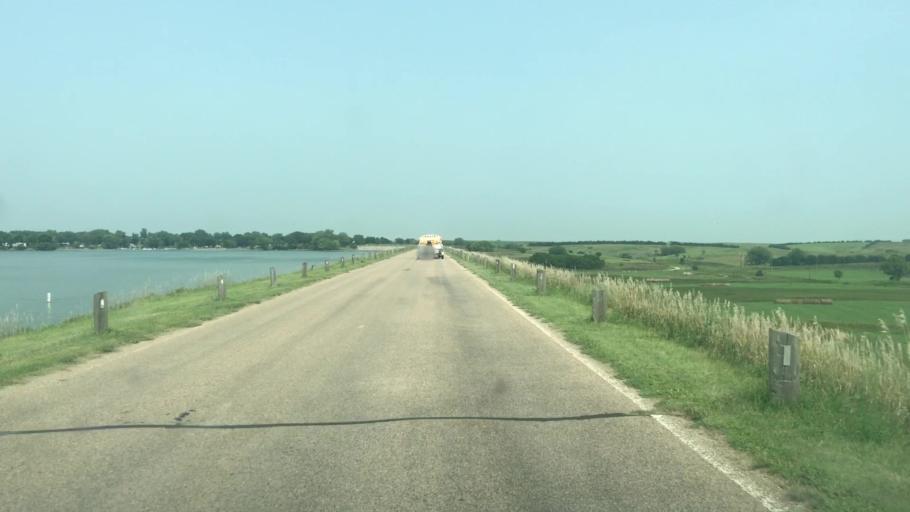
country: US
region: Nebraska
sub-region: Sherman County
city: Loup City
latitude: 41.3002
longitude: -98.8870
